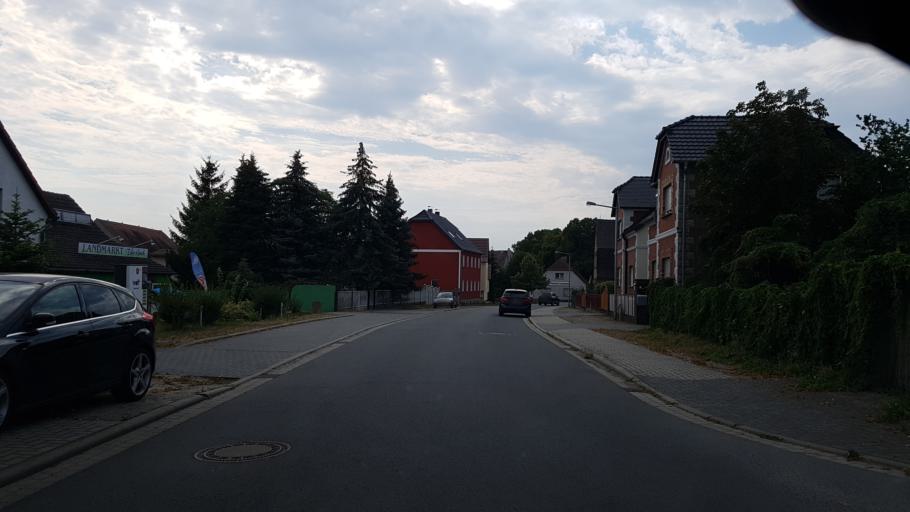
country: DE
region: Brandenburg
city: Lauchhammer
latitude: 51.5133
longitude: 13.7025
